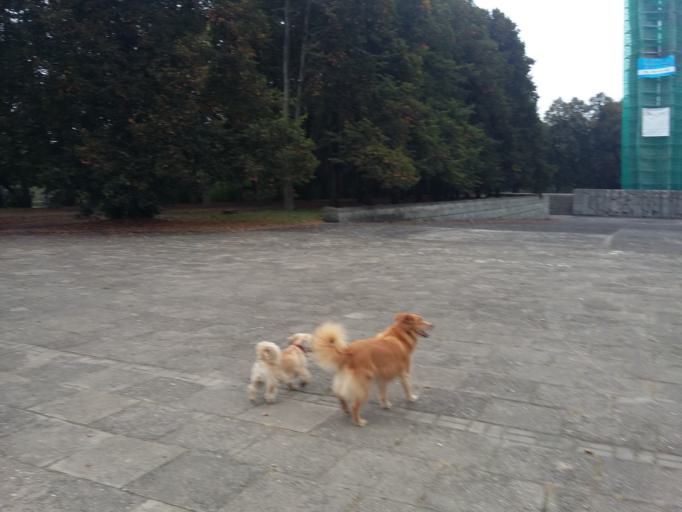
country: PL
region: Lodz Voivodeship
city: Lodz
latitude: 51.7656
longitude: 19.4160
